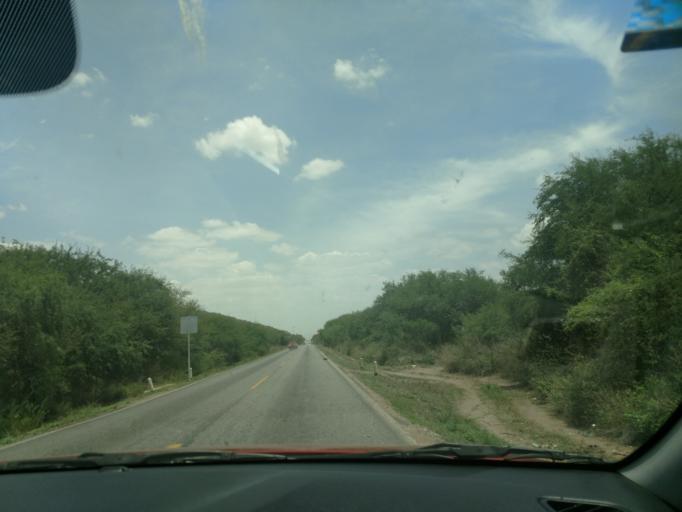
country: MX
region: San Luis Potosi
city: Ciudad Fernandez
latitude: 21.9829
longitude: -100.1148
